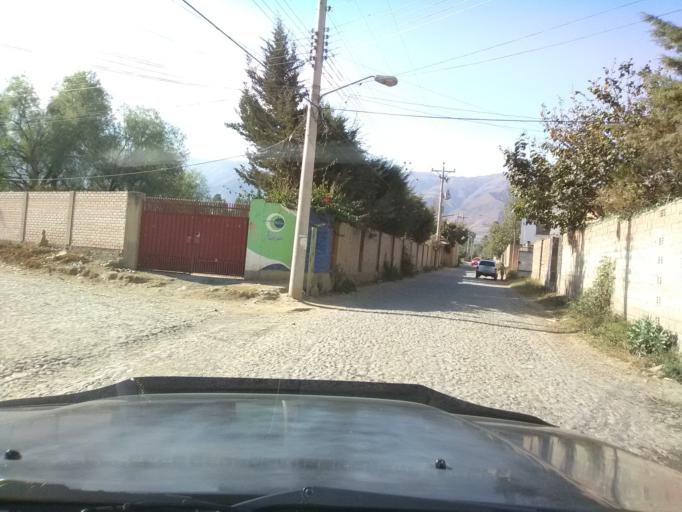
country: BO
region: Cochabamba
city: Cochabamba
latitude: -17.3618
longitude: -66.2124
